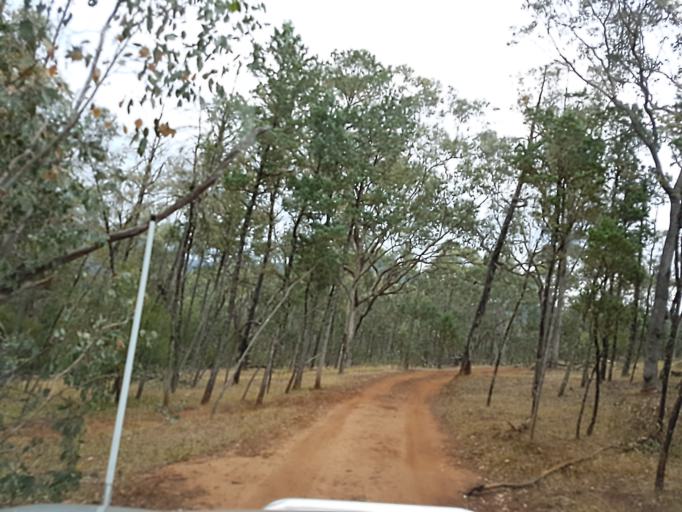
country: AU
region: New South Wales
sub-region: Snowy River
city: Jindabyne
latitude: -36.9393
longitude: 148.3987
